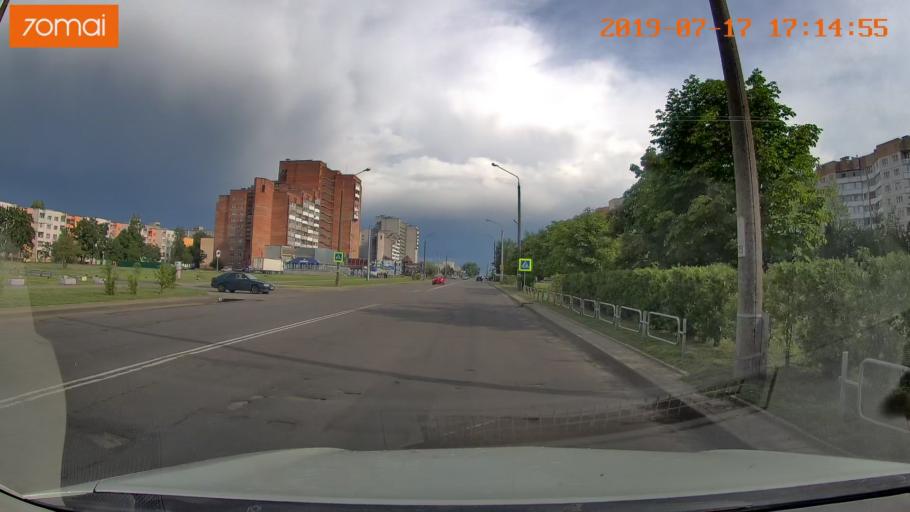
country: BY
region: Mogilev
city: Babruysk
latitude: 53.1728
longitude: 29.1891
